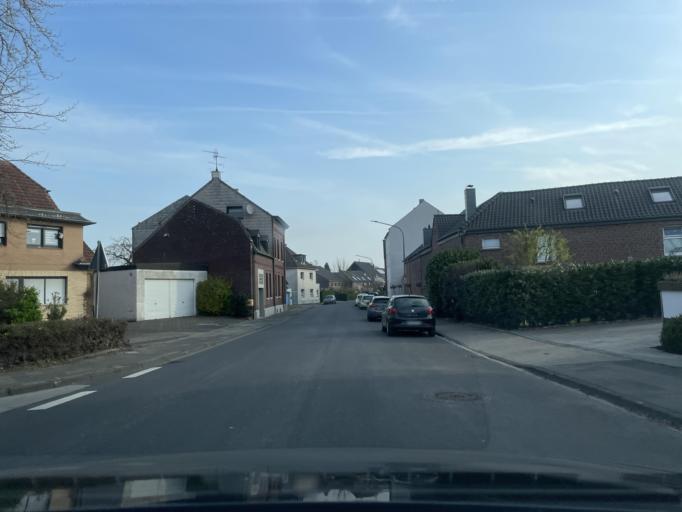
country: DE
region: North Rhine-Westphalia
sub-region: Regierungsbezirk Dusseldorf
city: Viersen
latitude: 51.2309
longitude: 6.4244
